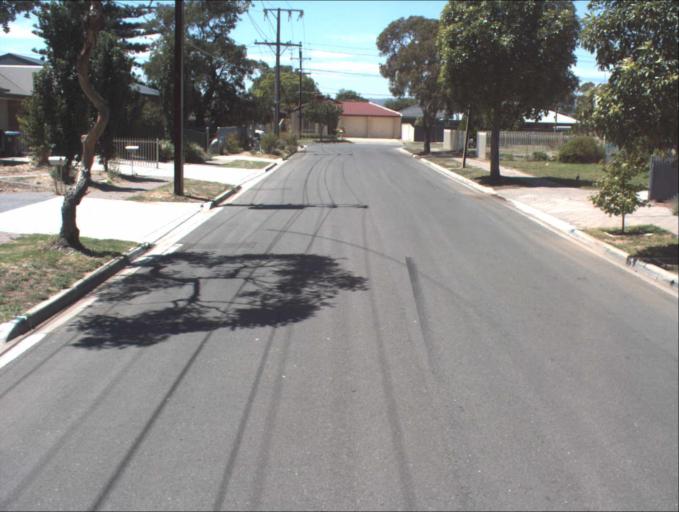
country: AU
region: South Australia
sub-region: Port Adelaide Enfield
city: Klemzig
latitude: -34.8697
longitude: 138.6237
